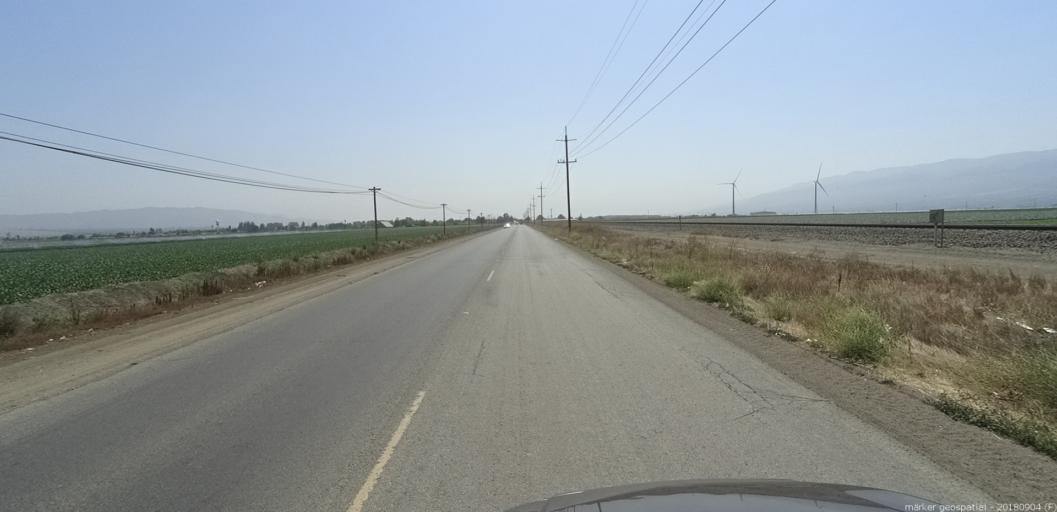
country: US
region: California
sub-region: Monterey County
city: Gonzales
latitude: 36.5163
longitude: -121.4572
